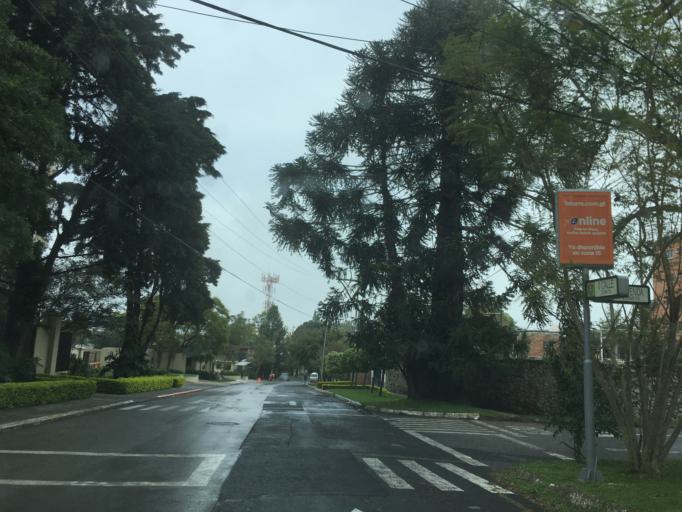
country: GT
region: Guatemala
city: Santa Catarina Pinula
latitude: 14.5877
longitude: -90.4946
